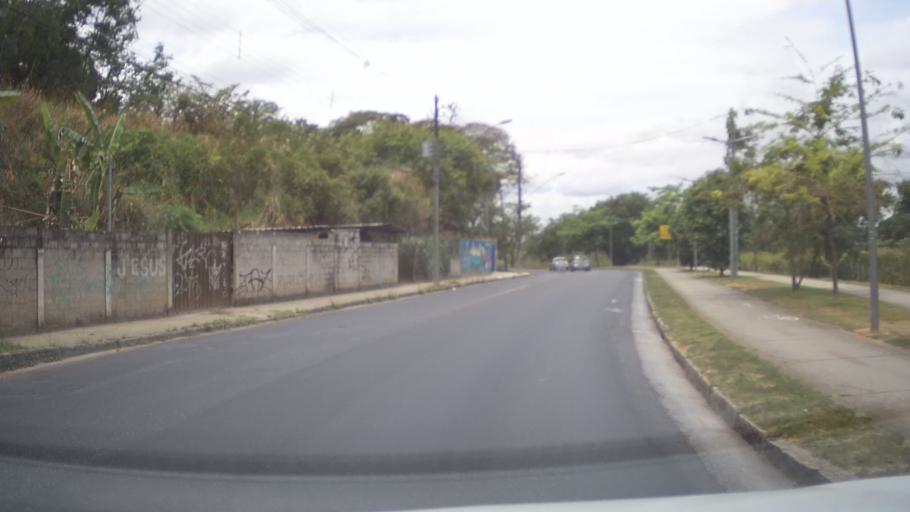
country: BR
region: Minas Gerais
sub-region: Contagem
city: Contagem
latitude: -19.8509
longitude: -44.0050
